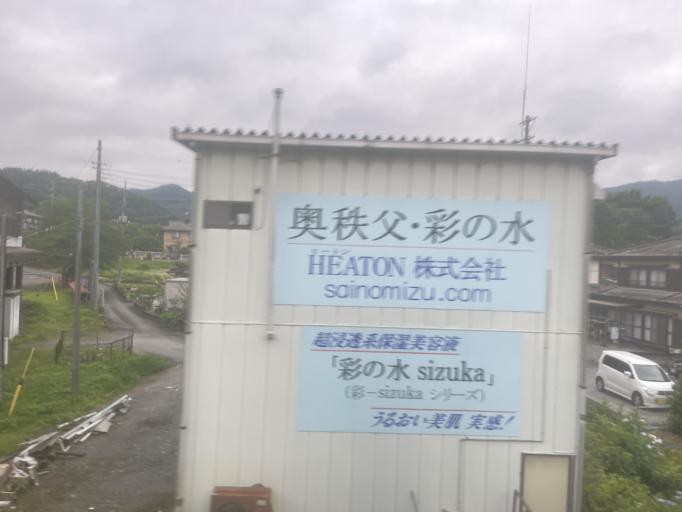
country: JP
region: Saitama
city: Kodamacho-kodamaminami
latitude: 36.1182
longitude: 139.1111
